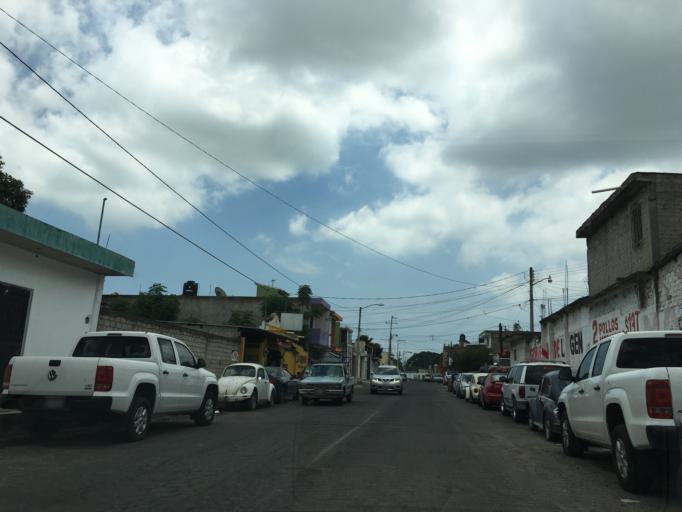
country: MX
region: Nayarit
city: Xalisco
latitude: 21.4728
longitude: -104.8877
